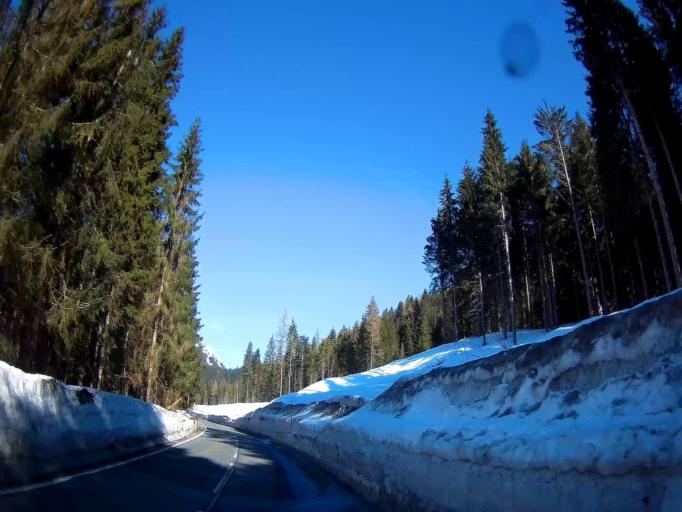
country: AT
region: Salzburg
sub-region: Politischer Bezirk Zell am See
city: Dienten am Hochkonig
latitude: 47.4056
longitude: 12.9762
